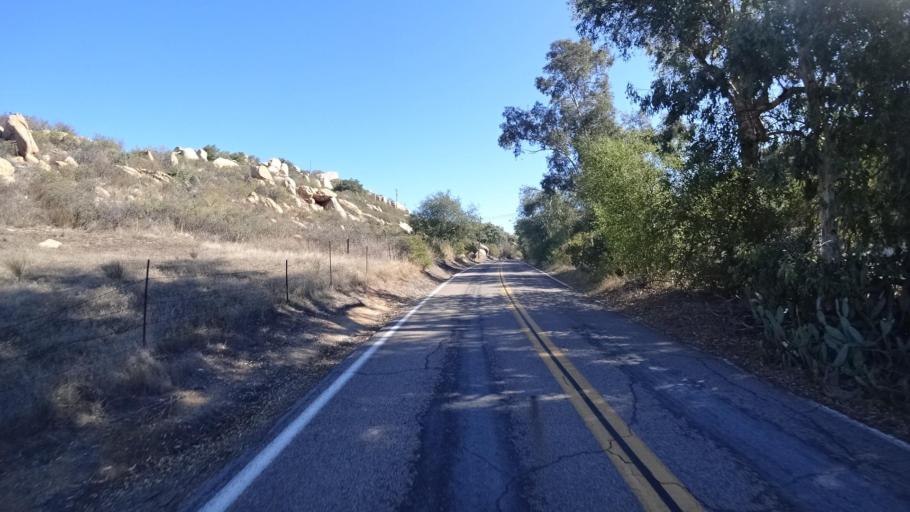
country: US
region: California
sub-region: San Diego County
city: Jamul
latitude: 32.7134
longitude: -116.7749
